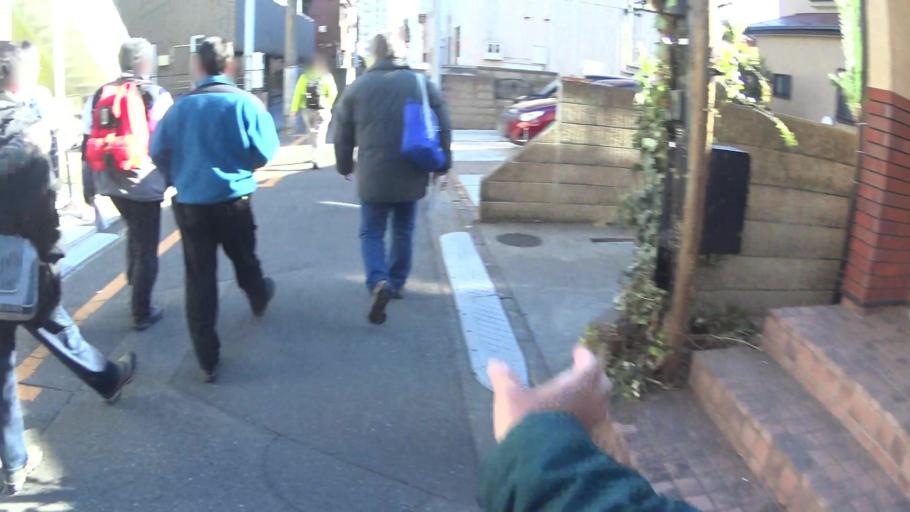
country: JP
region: Saitama
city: Shimotoda
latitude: 35.8451
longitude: 139.6737
